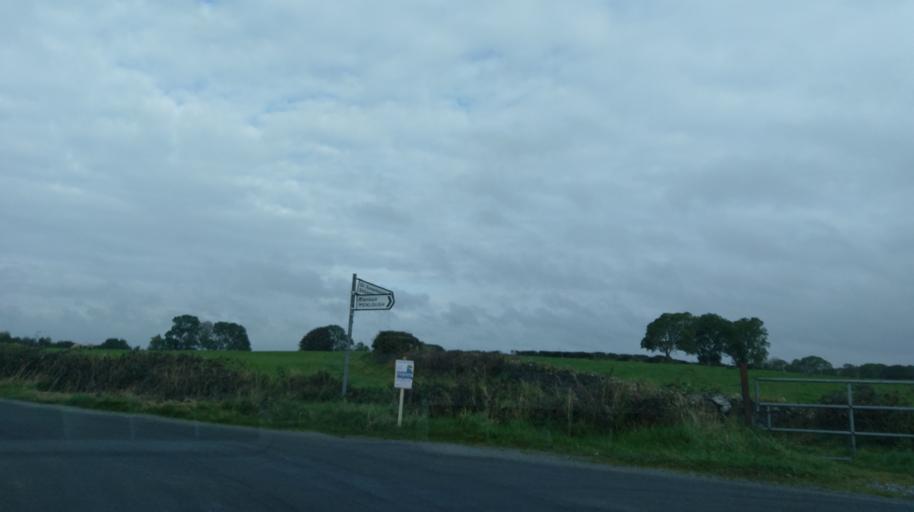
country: IE
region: Connaught
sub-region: County Galway
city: Athenry
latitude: 53.4636
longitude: -8.6313
